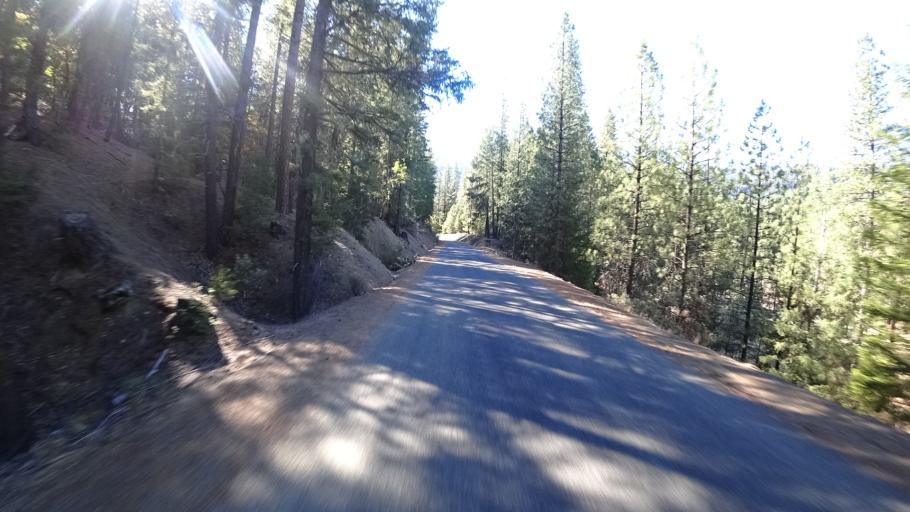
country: US
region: California
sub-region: Trinity County
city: Weaverville
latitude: 41.1198
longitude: -123.0922
